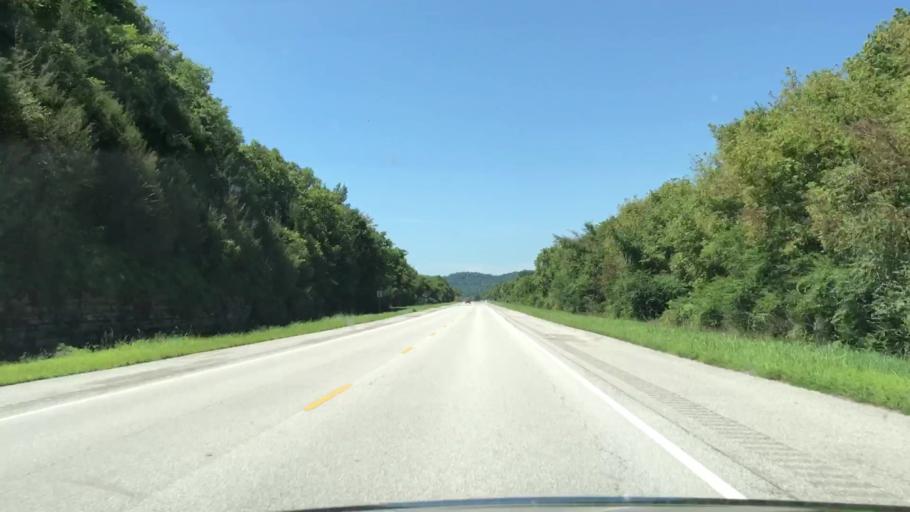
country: US
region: Tennessee
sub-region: Jackson County
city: Gainesboro
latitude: 36.4385
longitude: -85.6055
